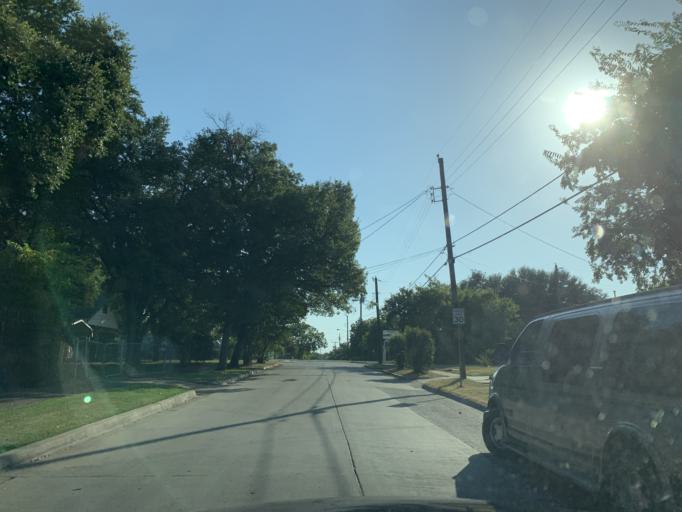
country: US
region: Texas
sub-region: Dallas County
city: Dallas
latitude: 32.7039
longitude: -96.7955
